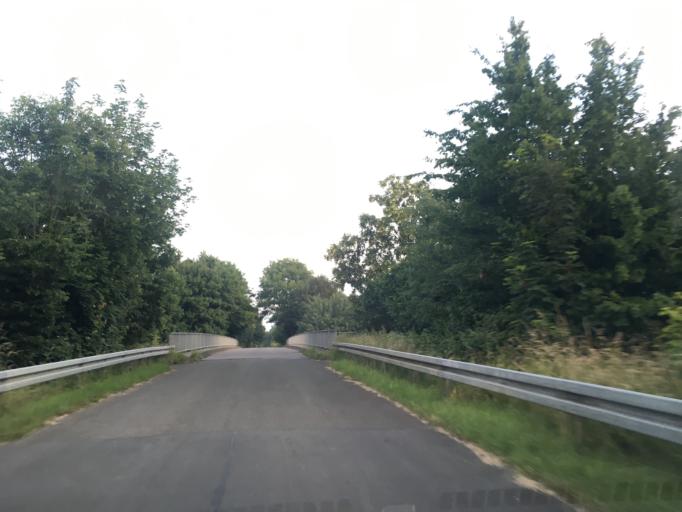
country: DE
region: North Rhine-Westphalia
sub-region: Regierungsbezirk Munster
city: Senden
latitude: 51.9139
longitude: 7.5403
